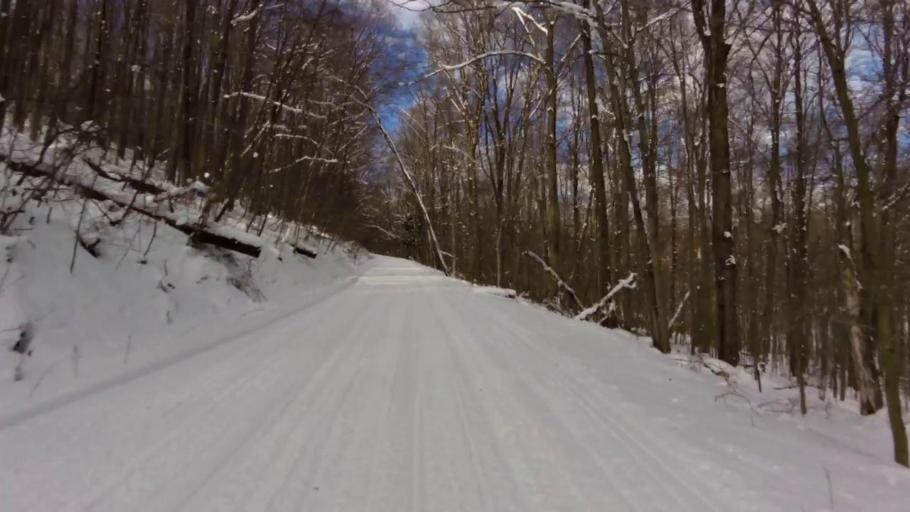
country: US
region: Pennsylvania
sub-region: McKean County
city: Bradford
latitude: 42.0345
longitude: -78.7034
